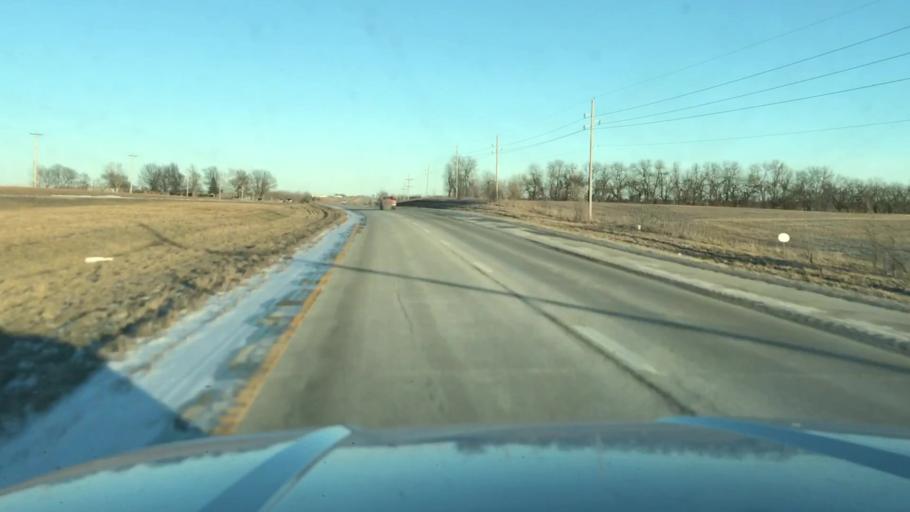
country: US
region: Missouri
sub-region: Clinton County
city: Cameron
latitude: 39.7544
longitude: -94.3314
